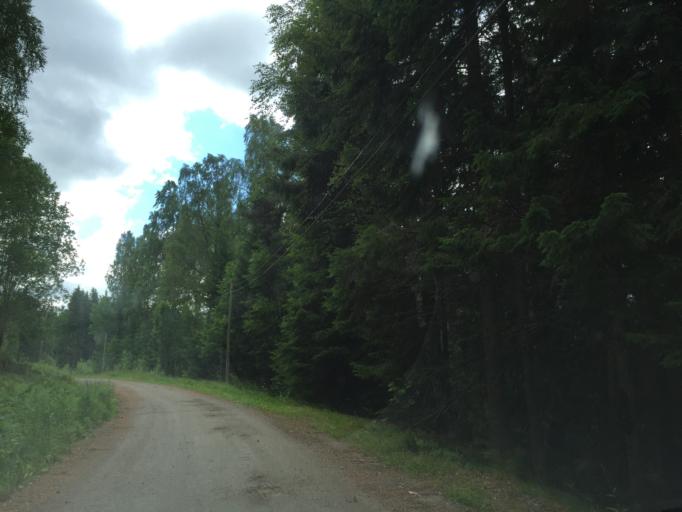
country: SE
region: OErebro
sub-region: Lekebergs Kommun
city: Fjugesta
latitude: 59.2771
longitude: 14.7832
